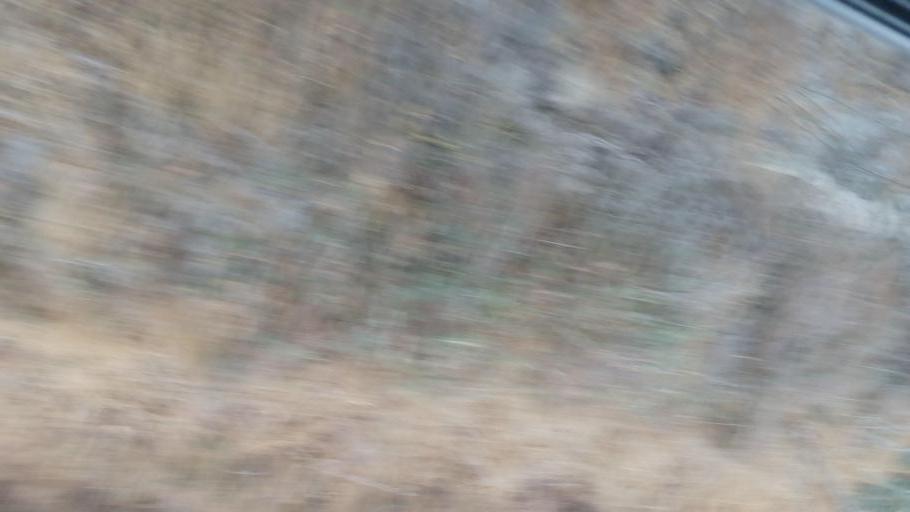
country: CY
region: Pafos
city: Tala
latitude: 34.9061
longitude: 32.5143
